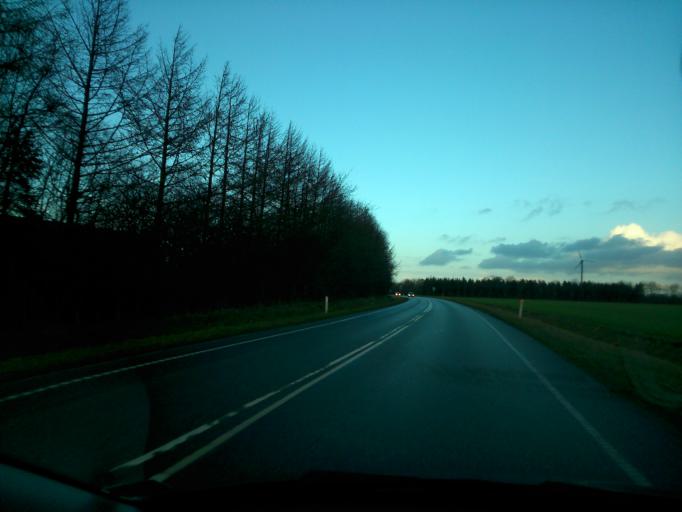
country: DK
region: Central Jutland
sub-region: Ringkobing-Skjern Kommune
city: Videbaek
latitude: 56.0876
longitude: 8.6487
